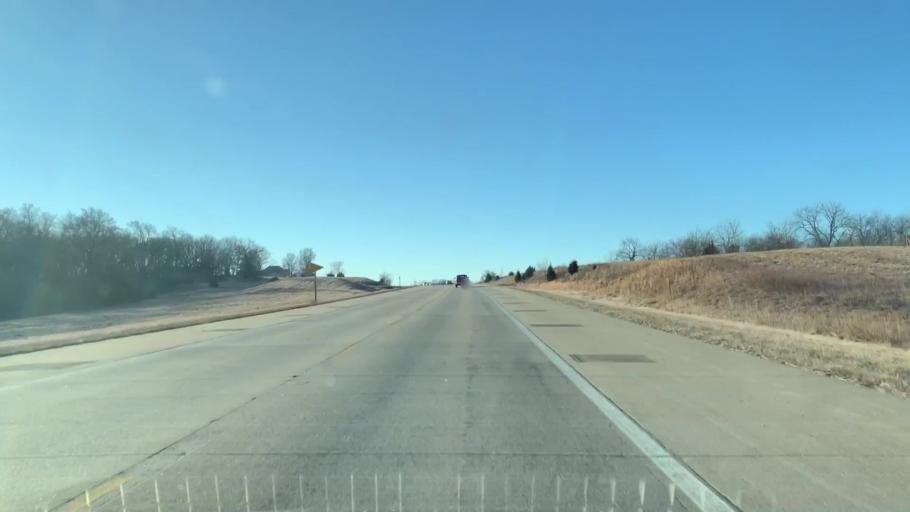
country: US
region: Kansas
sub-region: Crawford County
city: Arma
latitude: 37.5818
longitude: -94.7057
